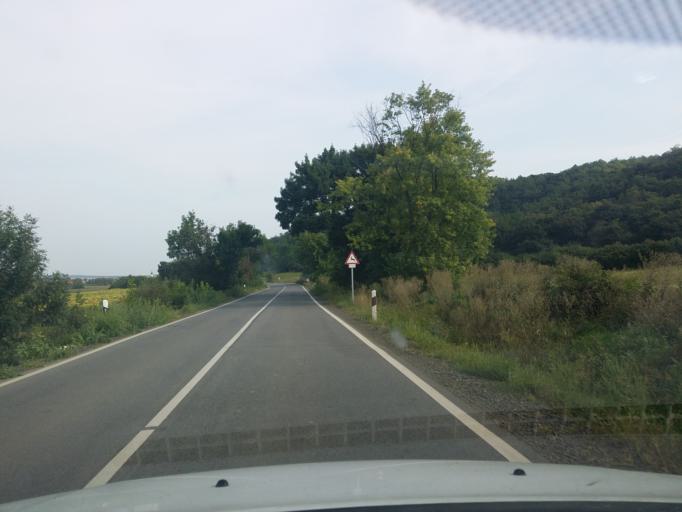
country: HU
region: Pest
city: Acsa
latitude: 47.7620
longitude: 19.3715
